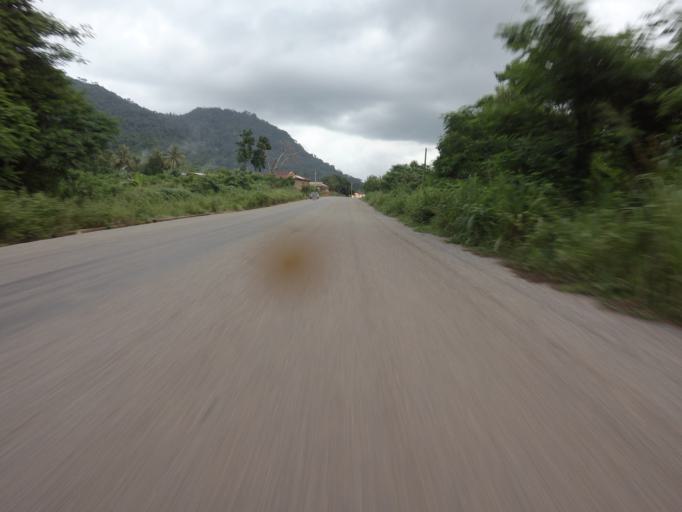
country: GH
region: Volta
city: Kpandu
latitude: 6.8015
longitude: 0.3729
